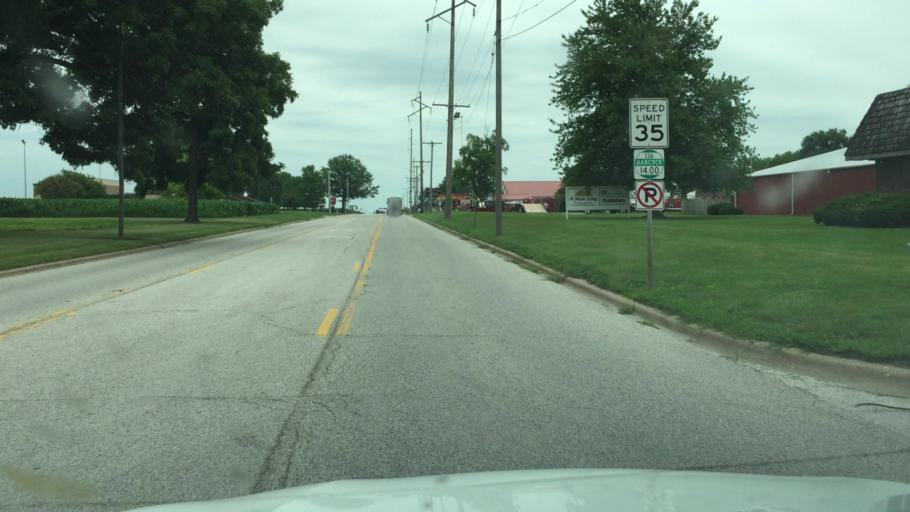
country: US
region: Illinois
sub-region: Hancock County
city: Carthage
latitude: 40.4161
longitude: -91.1242
